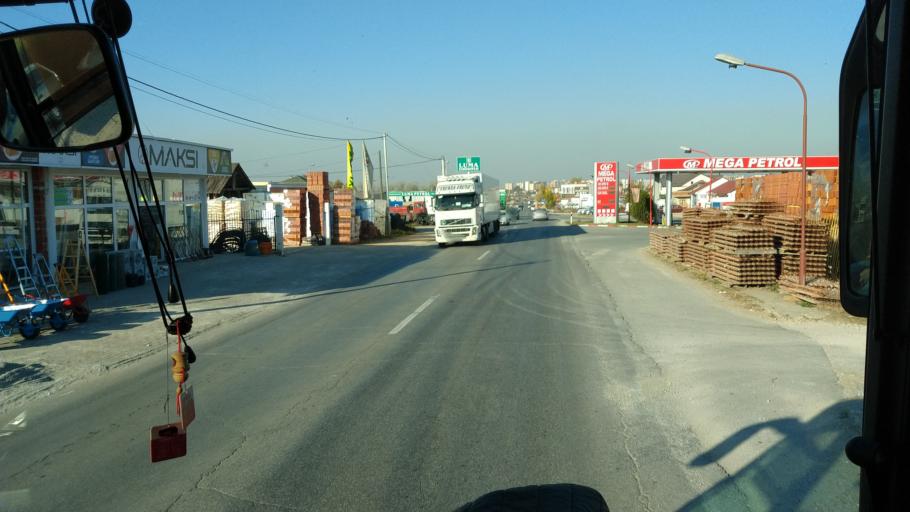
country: XK
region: Pristina
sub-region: Lipjan
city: Lipljan
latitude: 42.5061
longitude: 21.1109
